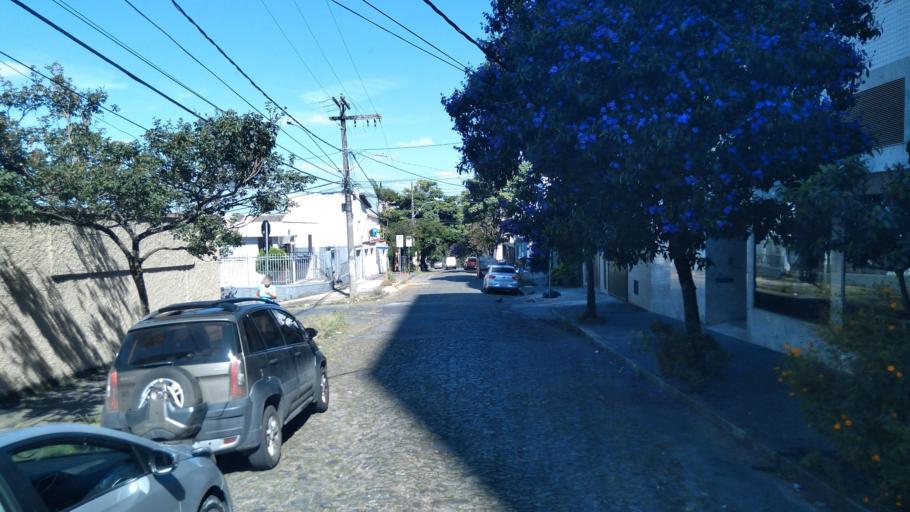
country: BR
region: Minas Gerais
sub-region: Belo Horizonte
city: Belo Horizonte
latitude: -19.8841
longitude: -43.9078
